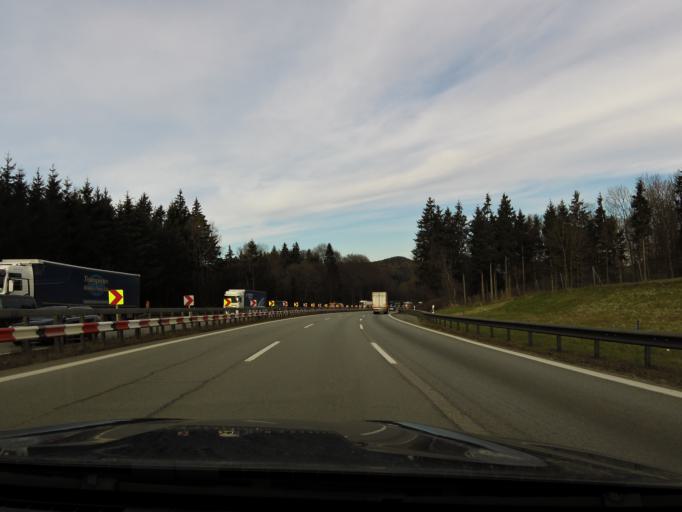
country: DE
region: Bavaria
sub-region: Upper Bavaria
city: Irschenberg
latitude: 47.8278
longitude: 11.8941
